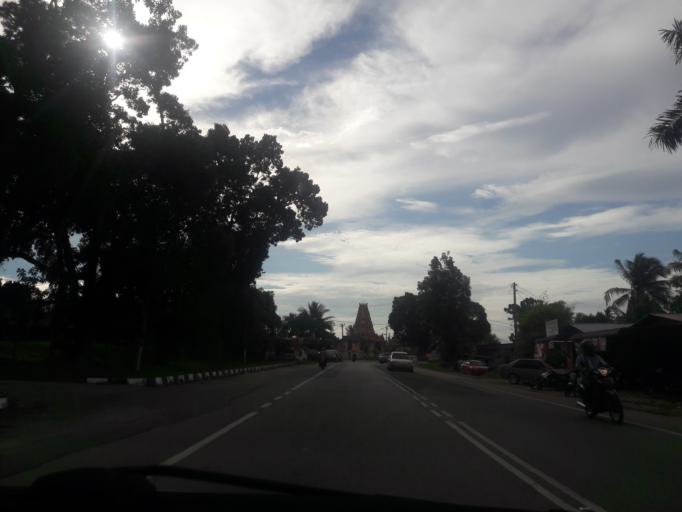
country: MY
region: Kedah
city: Sungai Petani
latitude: 5.6313
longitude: 100.5201
